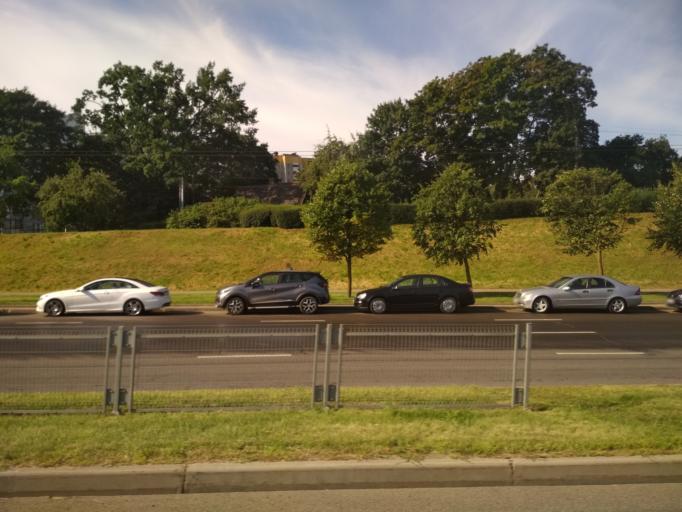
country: BY
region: Minsk
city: Minsk
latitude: 53.8865
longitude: 27.5482
